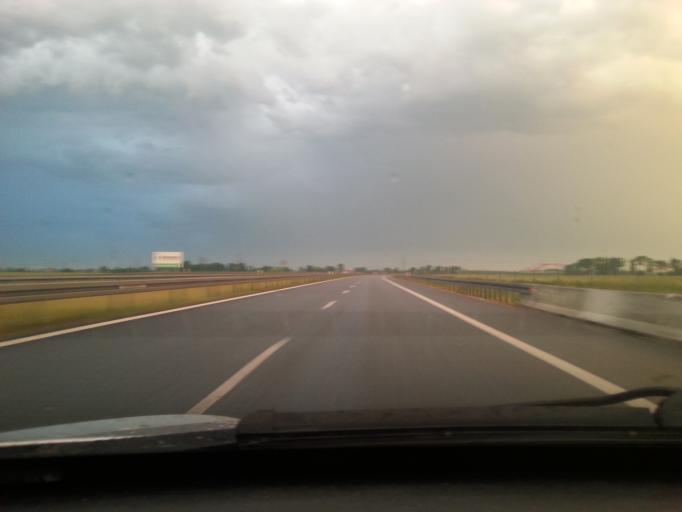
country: PL
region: Lodz Voivodeship
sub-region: Powiat pabianicki
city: Pabianice
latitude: 51.6946
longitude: 19.3414
